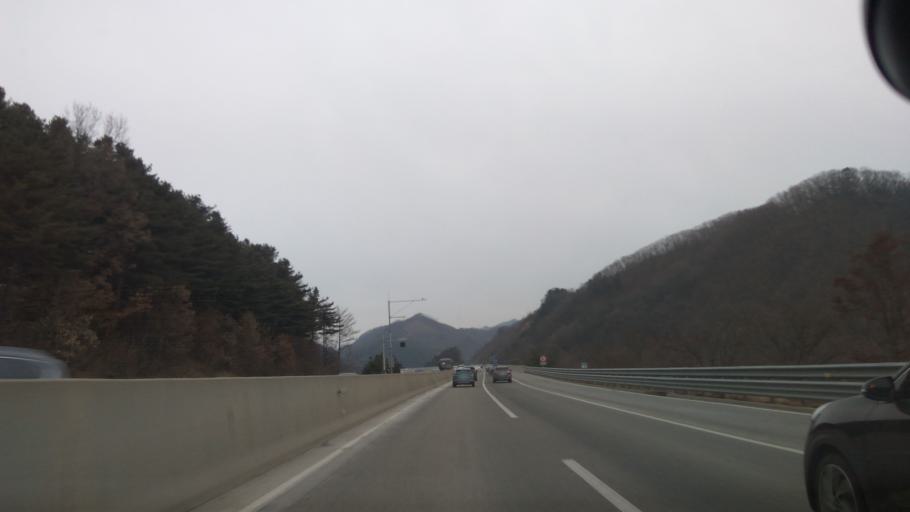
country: KR
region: Gyeonggi-do
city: Cheongpyeong
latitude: 37.6420
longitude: 127.4116
